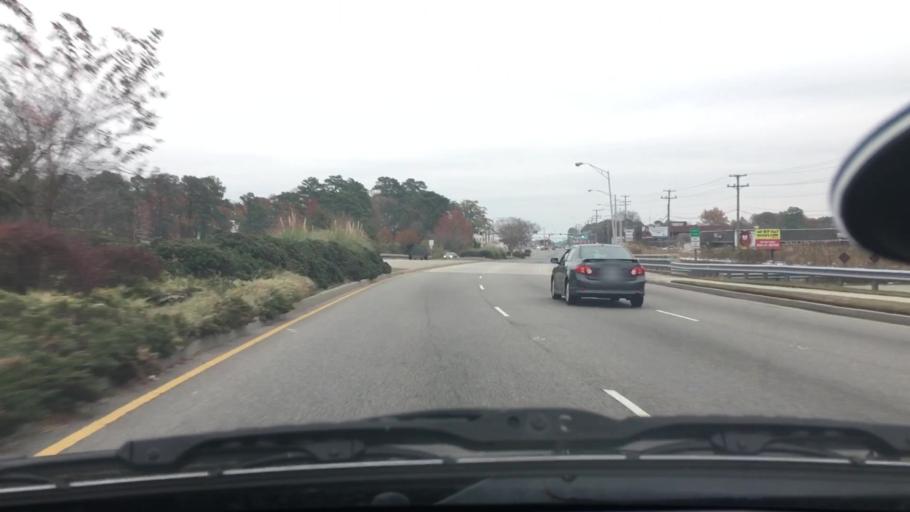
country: US
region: Virginia
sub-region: City of Norfolk
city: Norfolk
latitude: 36.8565
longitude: -76.2289
